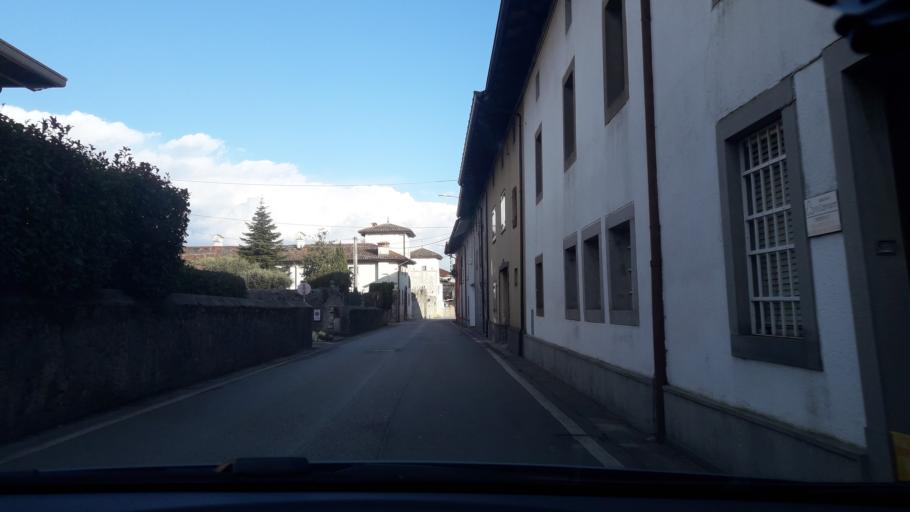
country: IT
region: Friuli Venezia Giulia
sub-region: Provincia di Udine
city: Reana del Rojale
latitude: 46.1442
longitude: 13.2362
